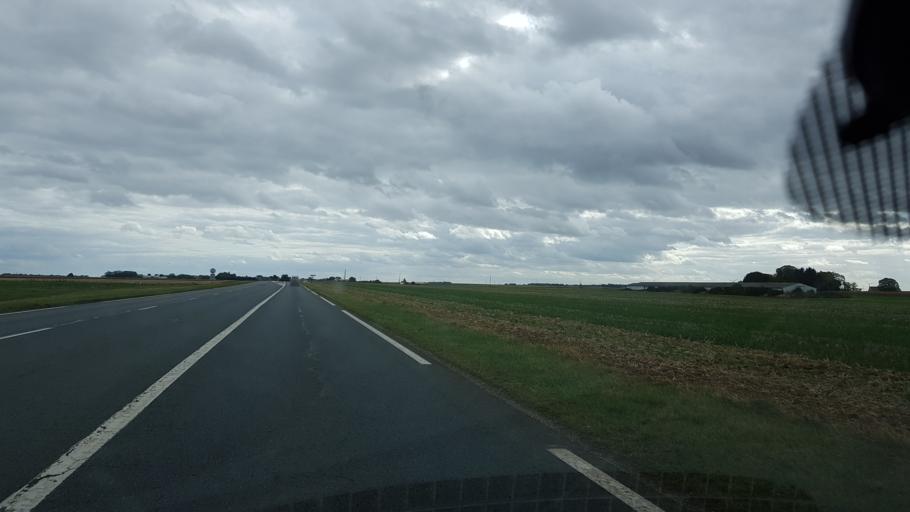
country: FR
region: Centre
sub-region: Departement du Loiret
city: Sermaises
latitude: 48.2727
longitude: 2.2100
